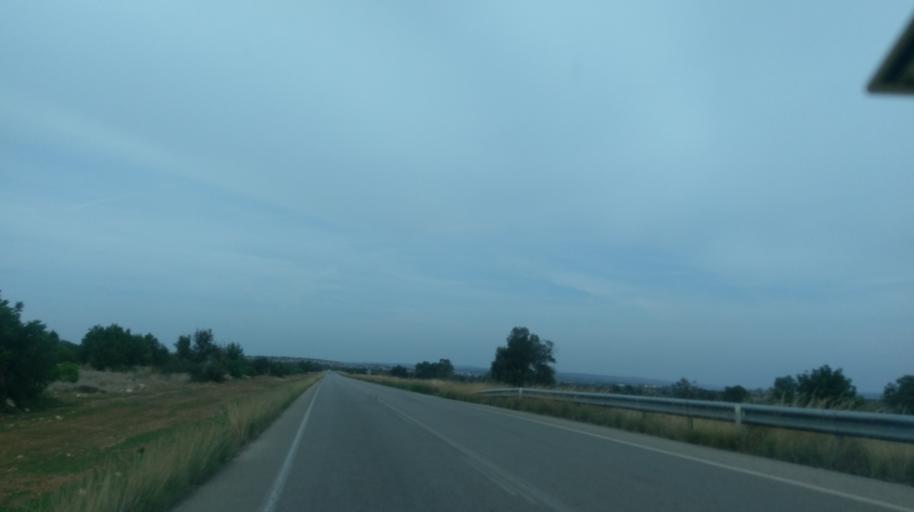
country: CY
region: Ammochostos
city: Leonarisso
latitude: 35.4036
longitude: 34.1065
